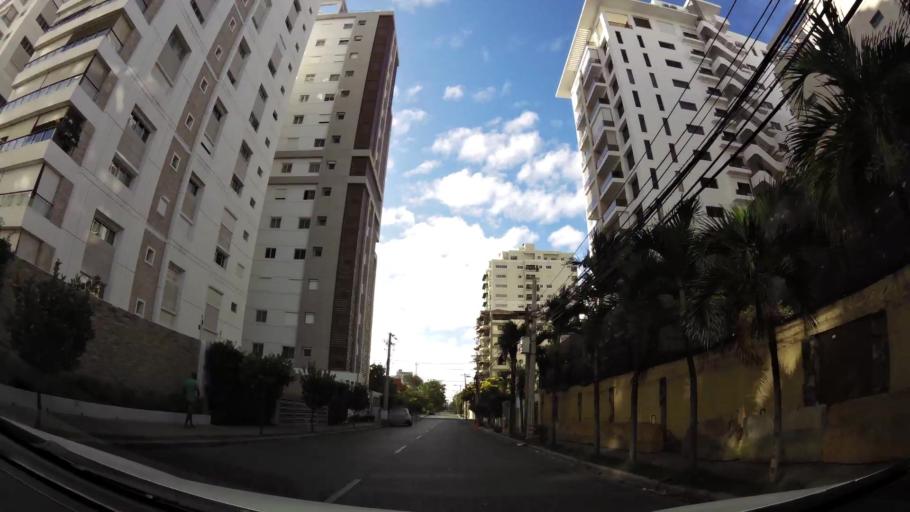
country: DO
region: Nacional
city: La Julia
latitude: 18.4756
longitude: -69.9408
